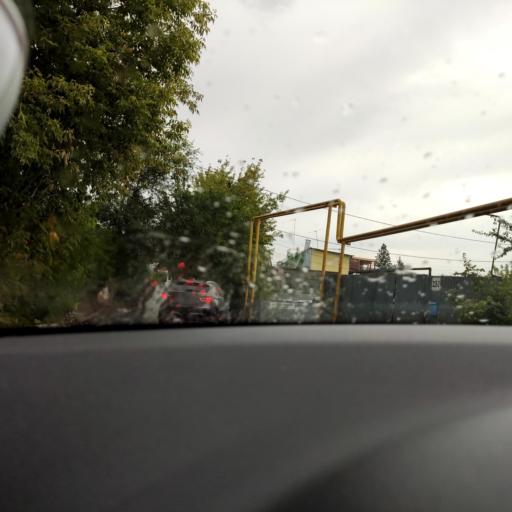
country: RU
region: Samara
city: Samara
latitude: 53.1742
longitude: 50.1565
